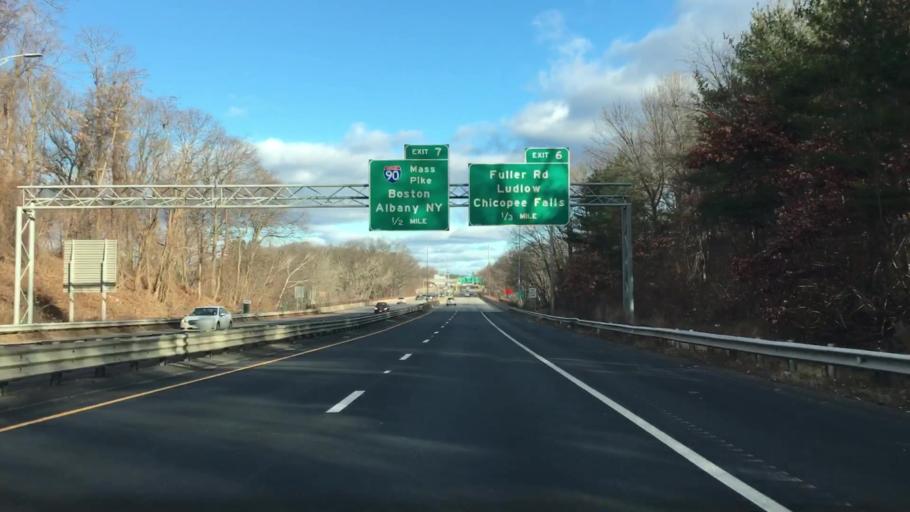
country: US
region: Massachusetts
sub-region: Hampden County
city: North Chicopee
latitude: 42.1555
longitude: -72.5486
